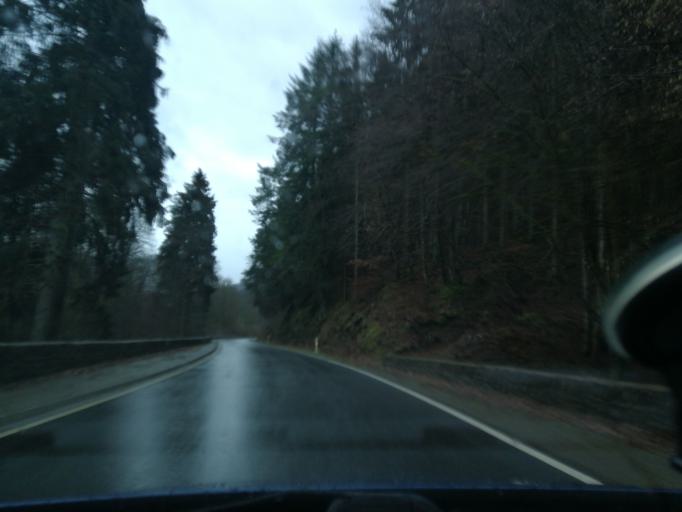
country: DE
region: Rheinland-Pfalz
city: Berglicht
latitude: 49.8185
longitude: 6.9505
